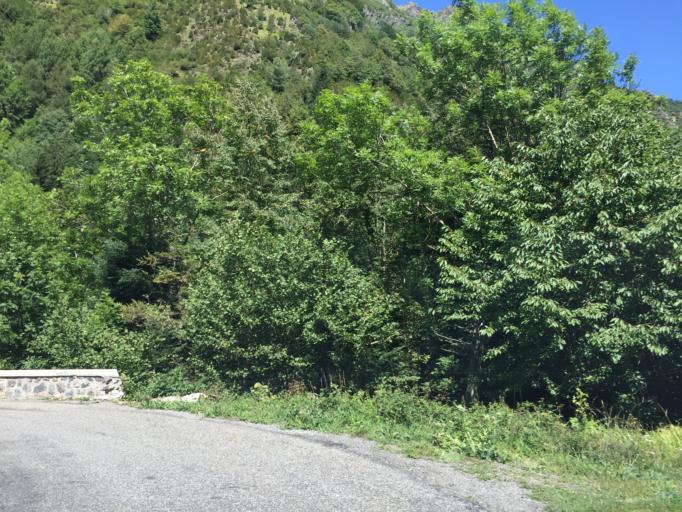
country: FR
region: Midi-Pyrenees
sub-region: Departement des Hautes-Pyrenees
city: Saint-Lary-Soulan
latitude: 42.8555
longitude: 0.3164
